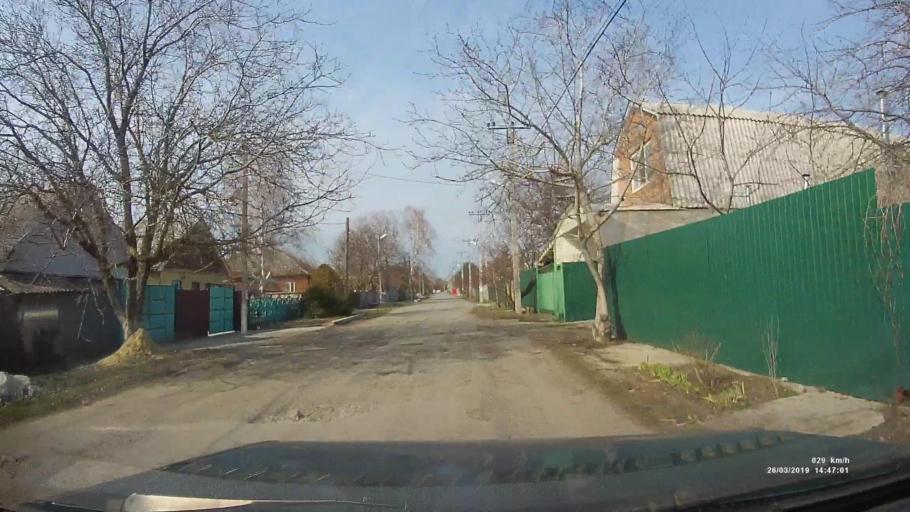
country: RU
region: Rostov
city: Novobessergenovka
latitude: 47.1892
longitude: 38.8596
